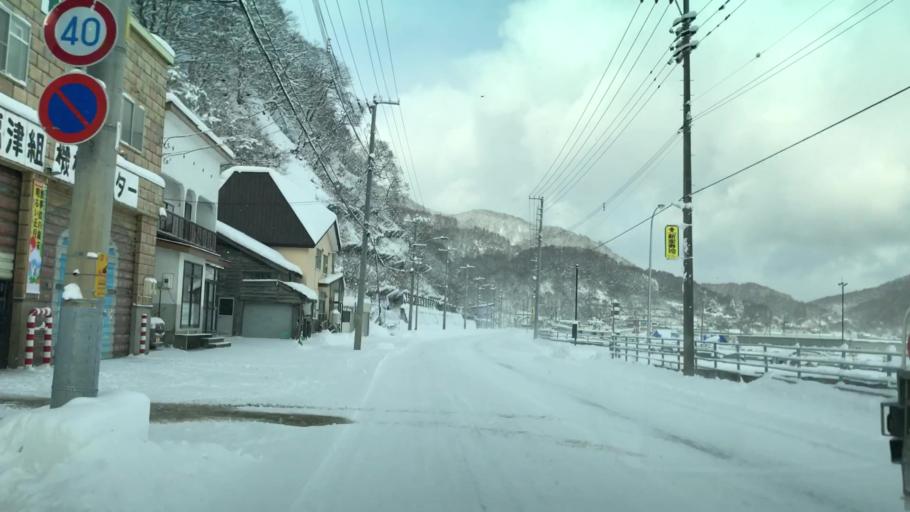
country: JP
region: Hokkaido
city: Yoichi
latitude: 43.2685
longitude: 140.6381
